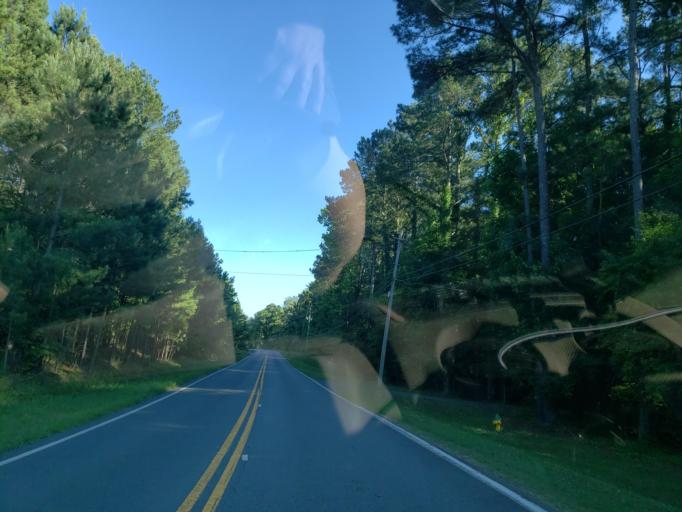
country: US
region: Georgia
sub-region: Floyd County
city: Shannon
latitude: 34.3767
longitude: -85.1331
